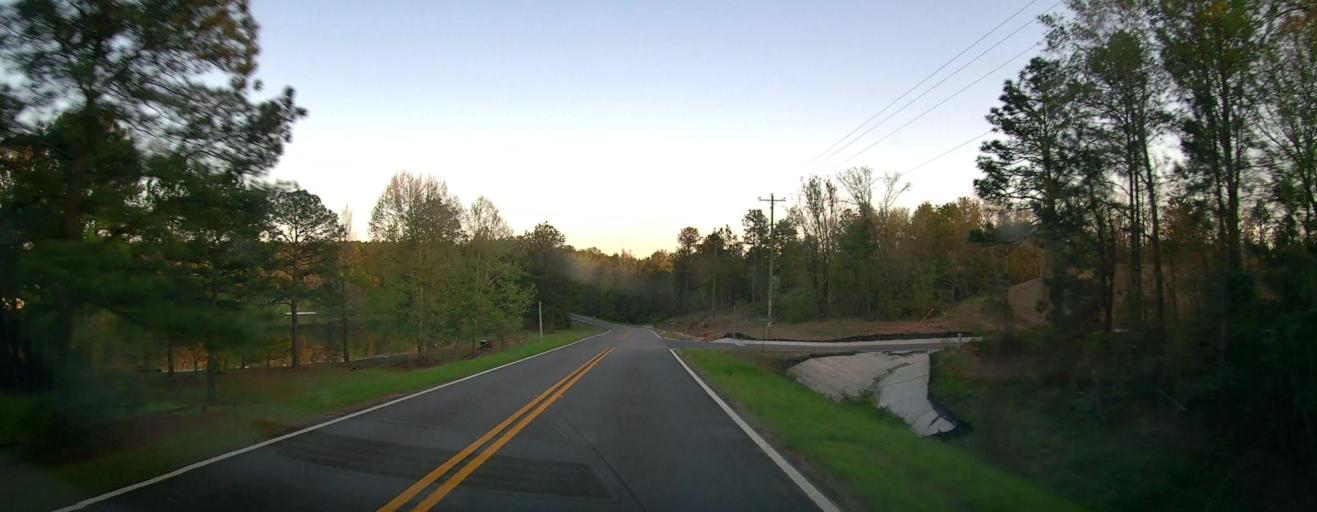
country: US
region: Georgia
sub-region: Marion County
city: Buena Vista
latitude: 32.4477
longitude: -84.6242
